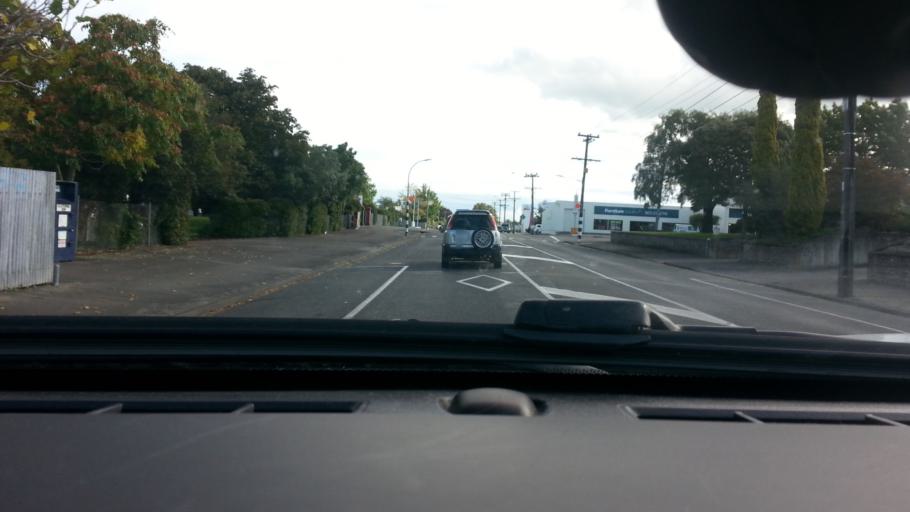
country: NZ
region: Wellington
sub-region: Masterton District
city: Masterton
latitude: -40.9557
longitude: 175.6546
